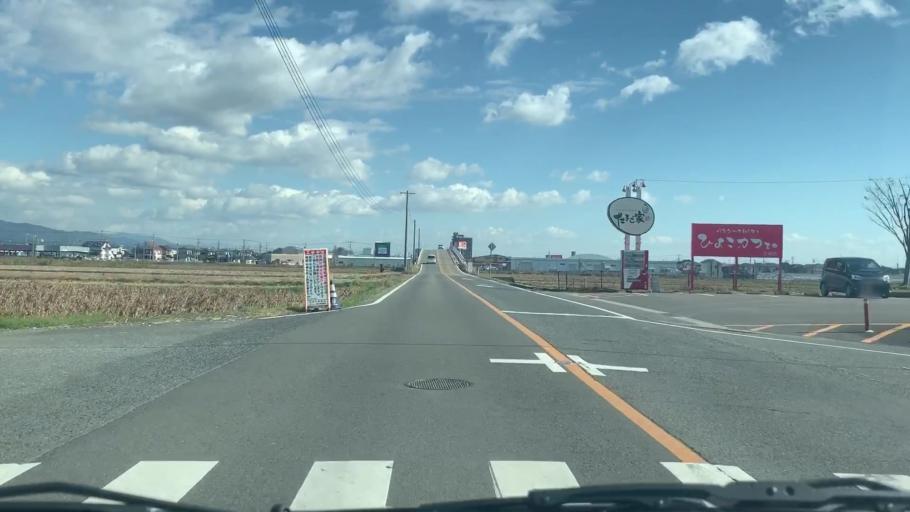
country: JP
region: Saga Prefecture
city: Saga-shi
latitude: 33.2764
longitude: 130.2108
